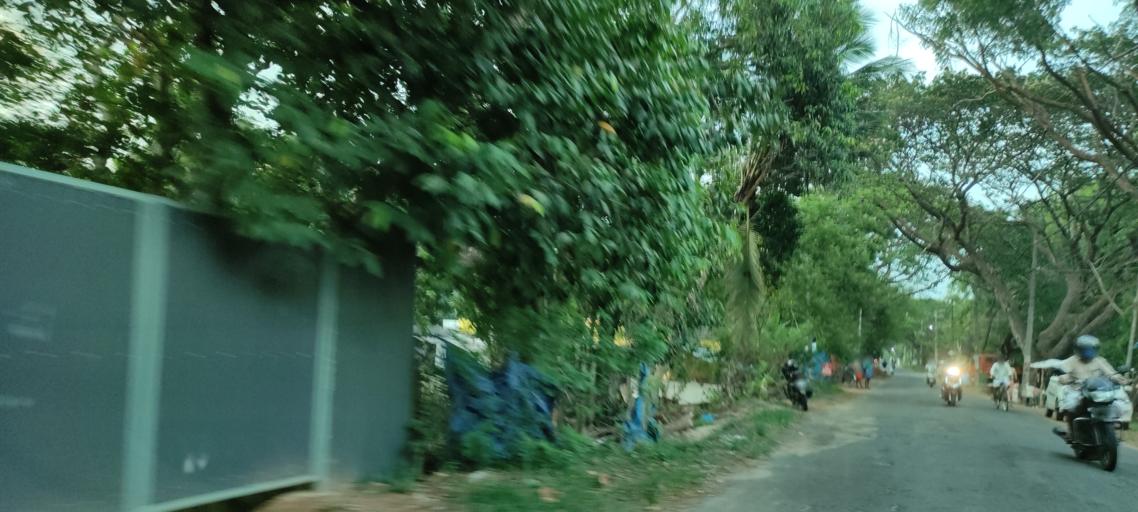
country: IN
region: Kerala
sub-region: Alappuzha
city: Shertallai
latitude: 9.6995
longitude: 76.3558
